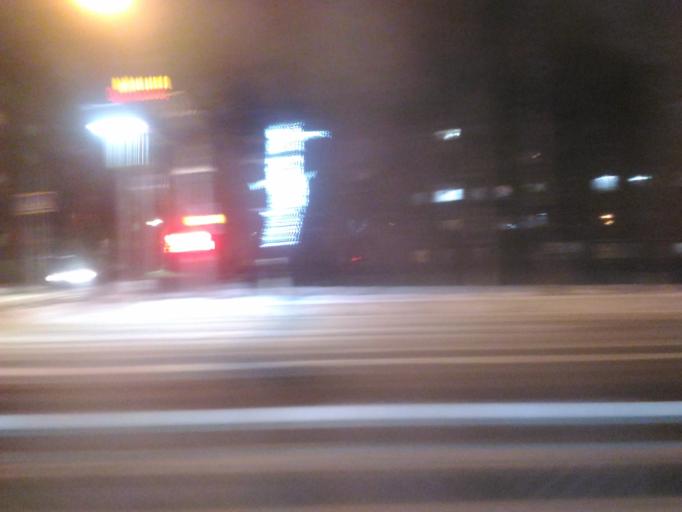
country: RU
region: Ulyanovsk
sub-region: Ulyanovskiy Rayon
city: Ulyanovsk
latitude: 54.3484
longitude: 48.3687
